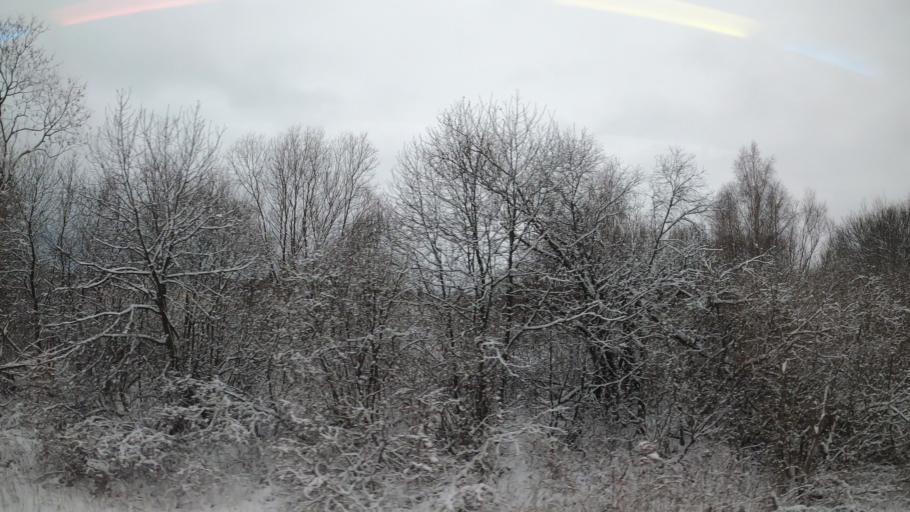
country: RU
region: Jaroslavl
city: Pereslavl'-Zalesskiy
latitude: 56.7147
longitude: 38.9101
